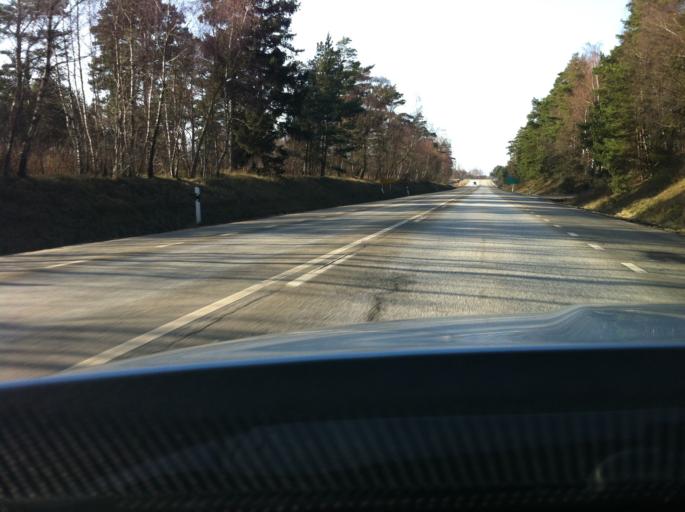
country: SE
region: Skane
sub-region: Kavlinge Kommun
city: Hofterup
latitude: 55.8237
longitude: 12.9438
